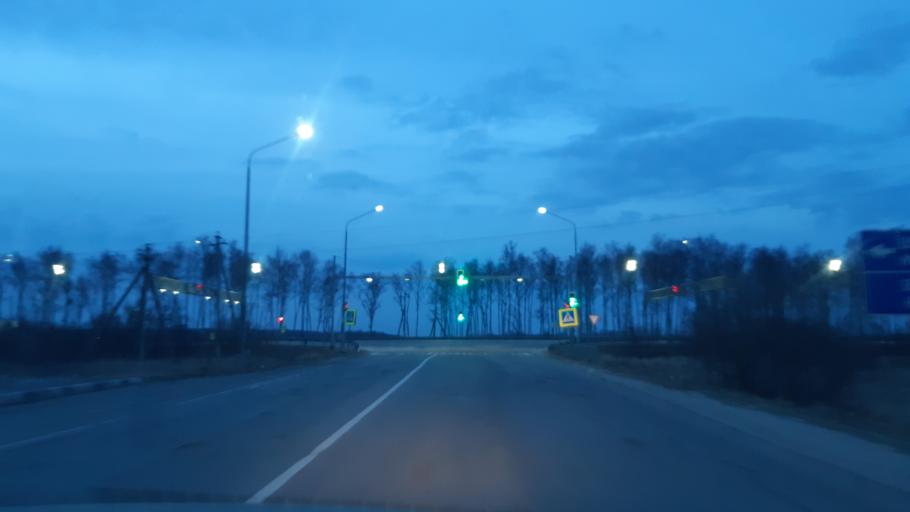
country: RU
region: Vladimir
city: Luknovo
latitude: 56.2375
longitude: 42.0341
